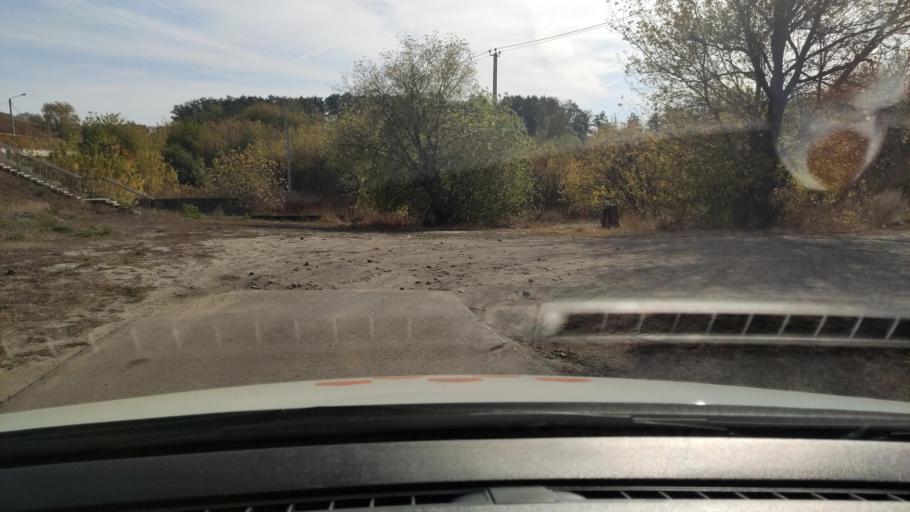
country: RU
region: Voronezj
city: Pridonskoy
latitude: 51.6654
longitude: 39.0868
